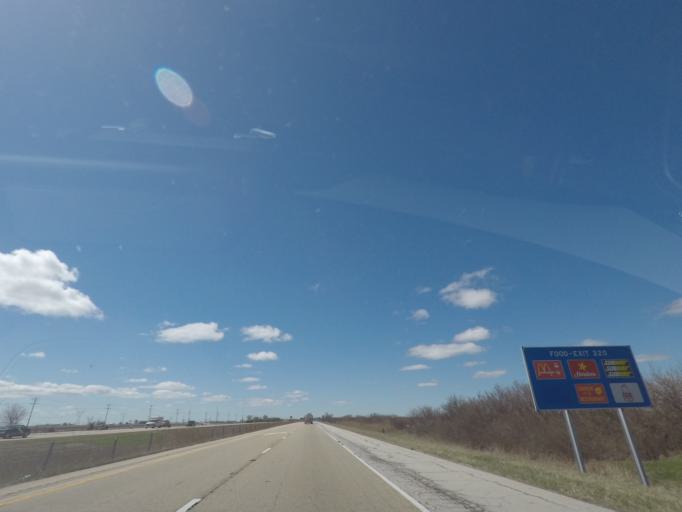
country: US
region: Illinois
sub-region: Livingston County
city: Dwight
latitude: 41.1283
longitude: -88.3845
